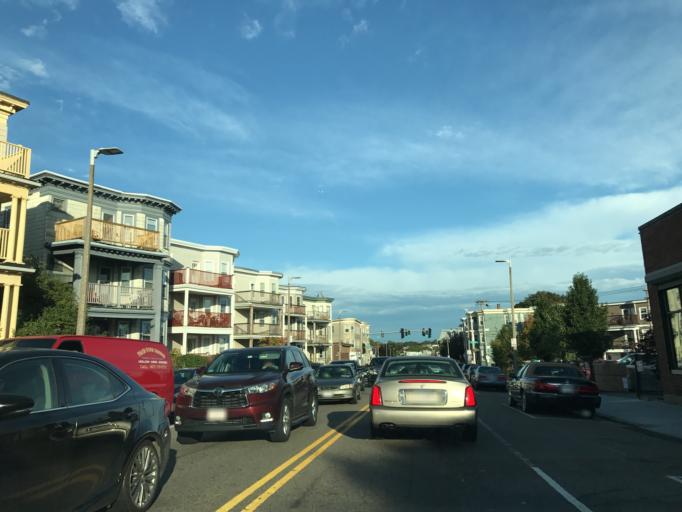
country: US
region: Massachusetts
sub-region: Suffolk County
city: South Boston
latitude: 42.2954
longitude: -71.0537
